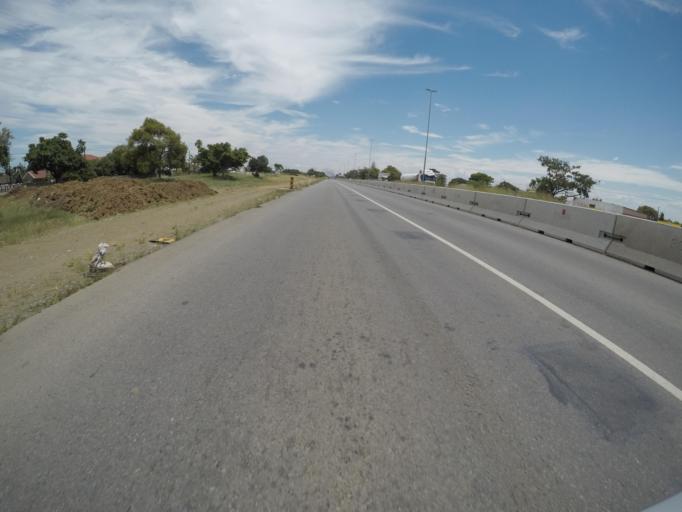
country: ZA
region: Eastern Cape
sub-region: Buffalo City Metropolitan Municipality
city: East London
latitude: -33.0360
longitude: 27.8537
